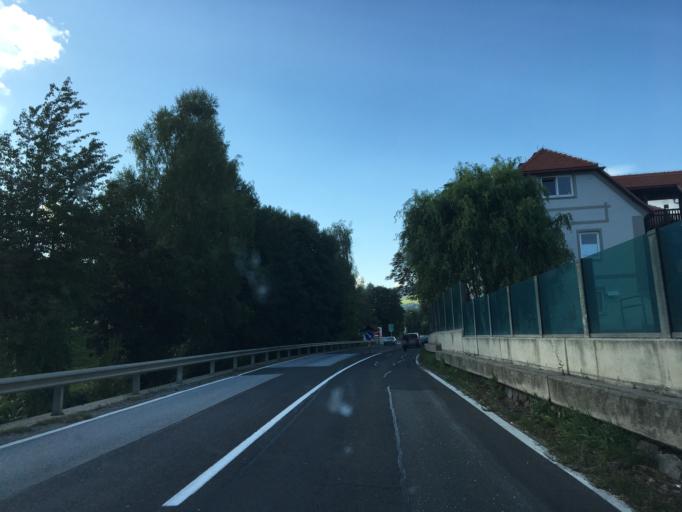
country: AT
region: Styria
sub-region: Politischer Bezirk Murau
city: Sankt Marein bei Neumarkt
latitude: 47.0655
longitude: 14.4307
